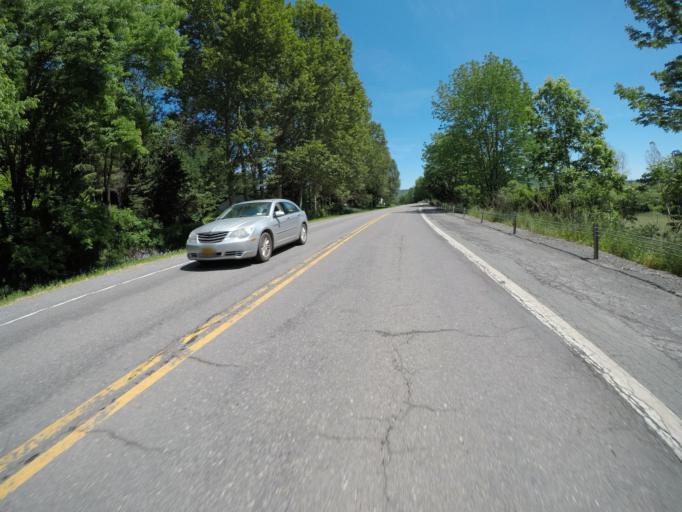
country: US
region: New York
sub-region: Delaware County
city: Delhi
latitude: 42.2034
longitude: -74.9860
